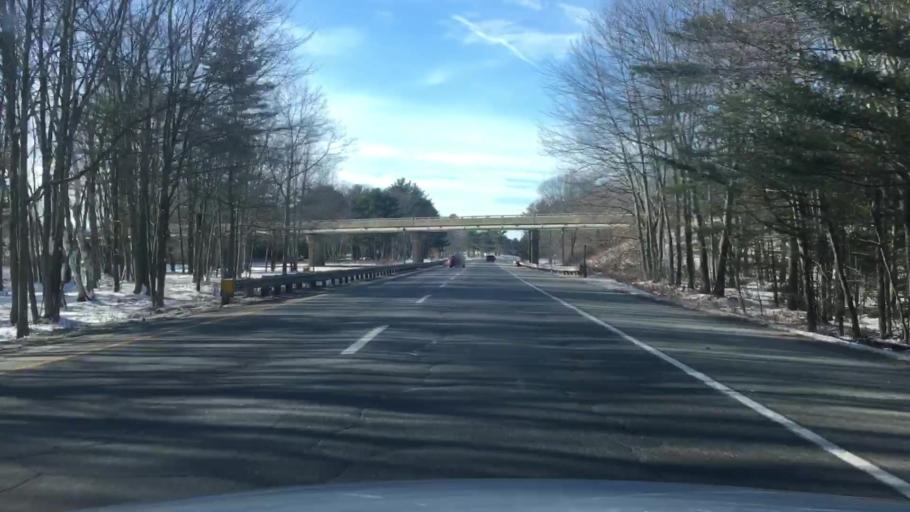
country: US
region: Maine
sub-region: Cumberland County
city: Brunswick
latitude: 43.9131
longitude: -69.9060
